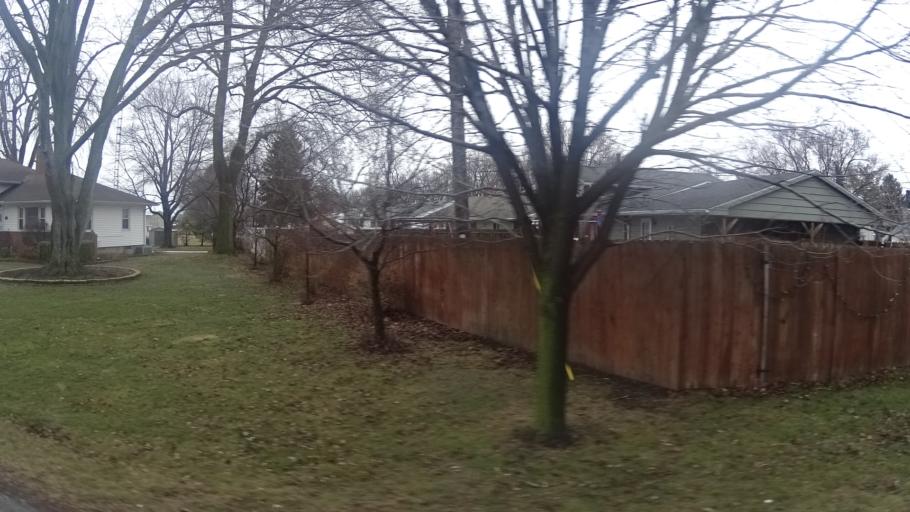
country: US
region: Ohio
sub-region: Erie County
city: Sandusky
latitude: 41.4247
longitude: -82.6578
